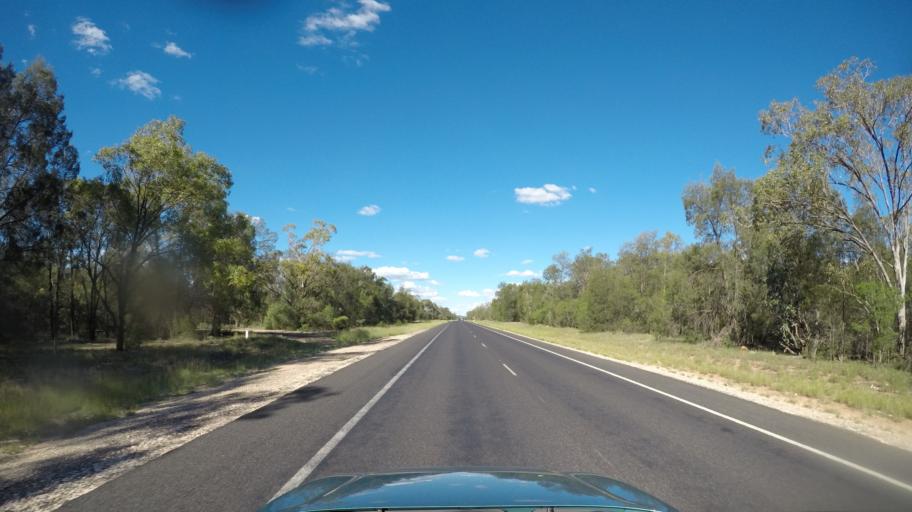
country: AU
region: Queensland
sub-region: Goondiwindi
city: Goondiwindi
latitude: -28.0570
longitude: 150.7711
